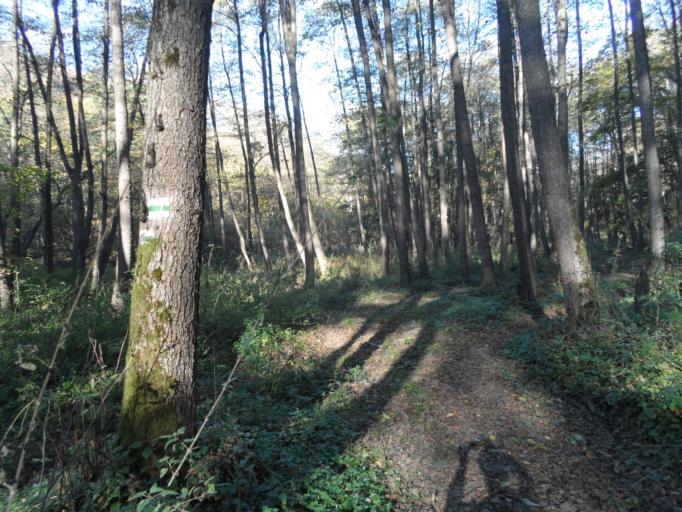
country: HU
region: Veszprem
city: Ajka
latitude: 47.1922
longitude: 17.5845
